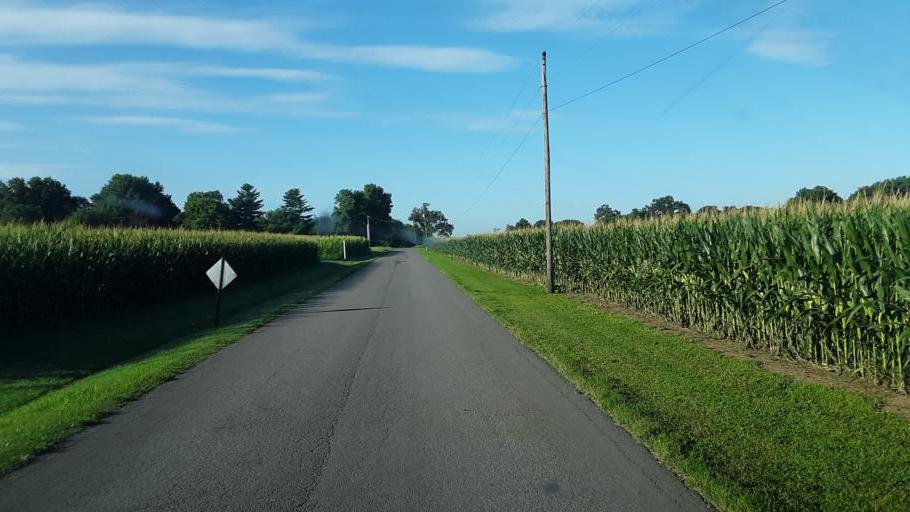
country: US
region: Kentucky
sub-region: Todd County
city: Guthrie
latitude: 36.7252
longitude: -87.1689
